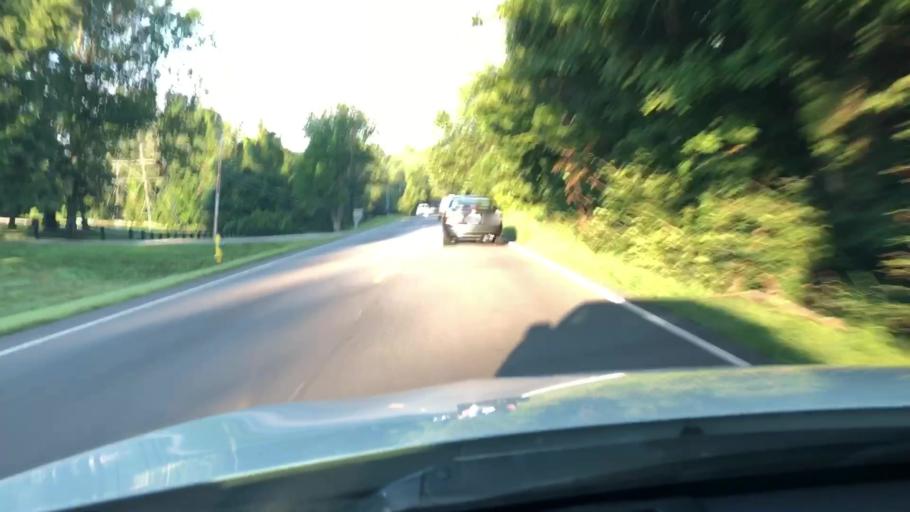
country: US
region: Kentucky
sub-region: Jefferson County
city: Middletown
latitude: 38.2201
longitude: -85.5157
